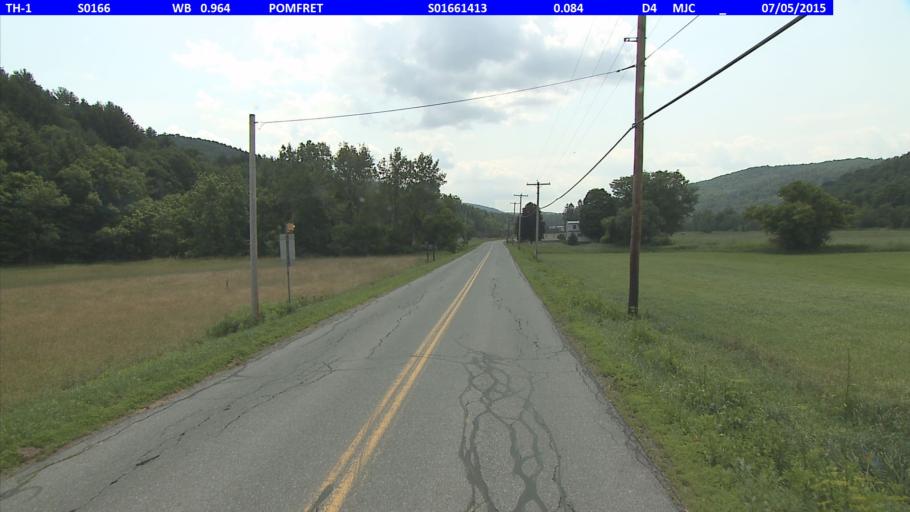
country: US
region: Vermont
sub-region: Windsor County
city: Woodstock
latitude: 43.6517
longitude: -72.5273
